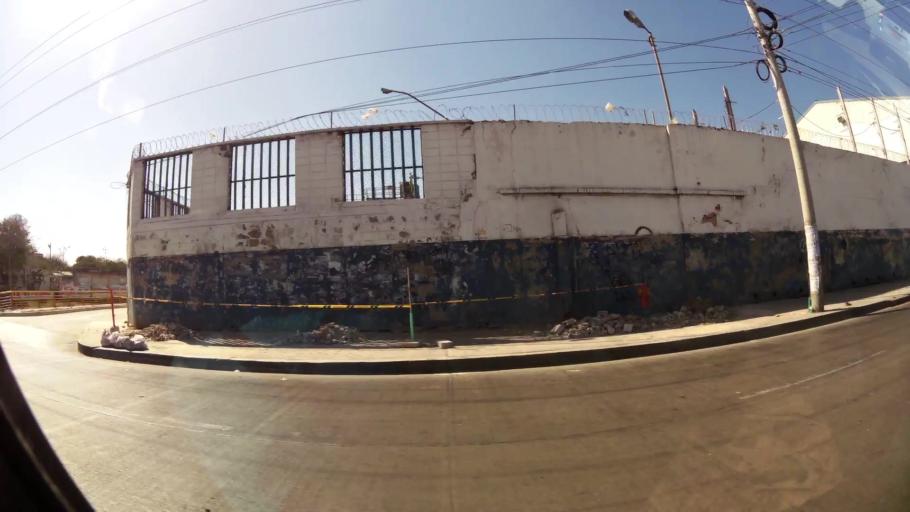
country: CO
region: Atlantico
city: Barranquilla
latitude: 10.9594
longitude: -74.7851
